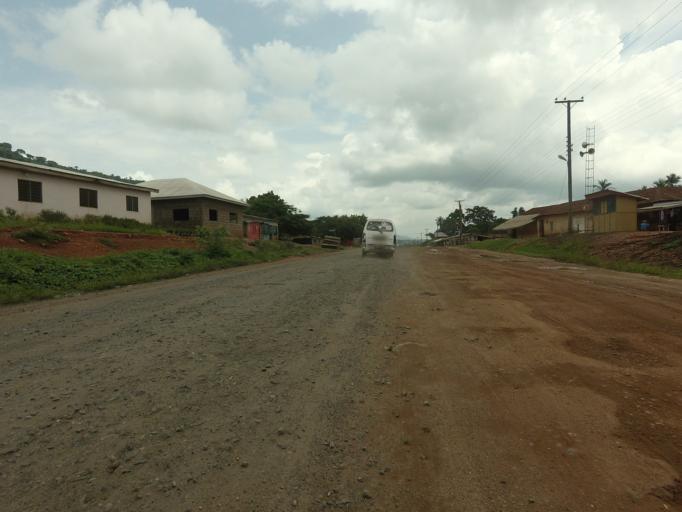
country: GH
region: Volta
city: Ho
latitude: 6.6239
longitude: 0.3094
